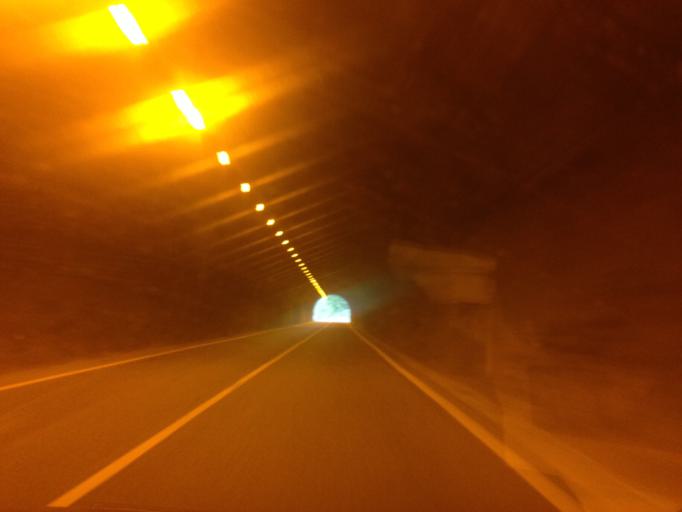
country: FR
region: Rhone-Alpes
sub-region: Departement de la Savoie
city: Tignes
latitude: 45.5054
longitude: 6.9279
